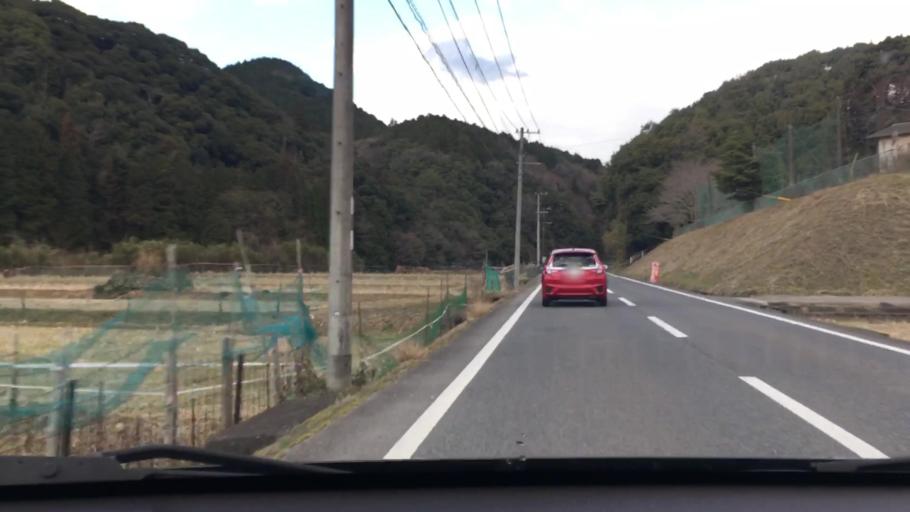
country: JP
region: Oita
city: Bungo-Takada-shi
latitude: 33.4512
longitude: 131.3929
